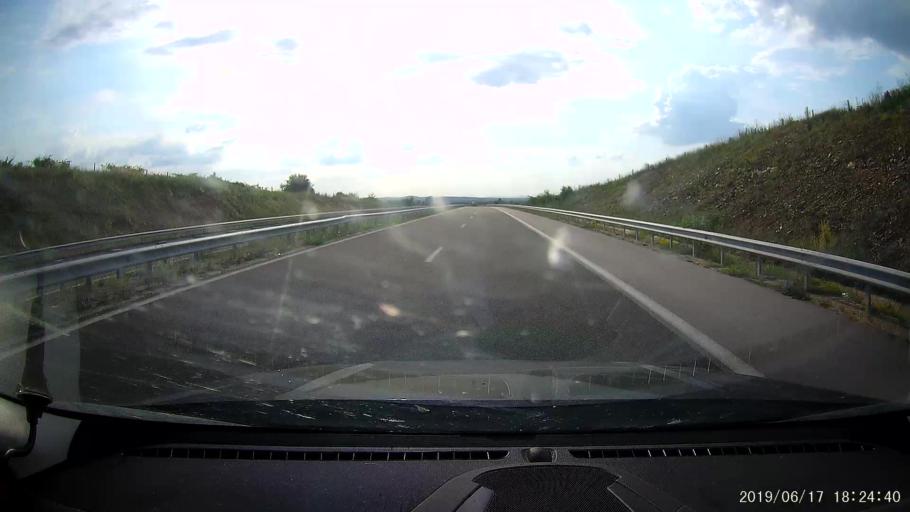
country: BG
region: Khaskovo
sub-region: Obshtina Dimitrovgrad
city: Dimitrovgrad
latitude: 41.9867
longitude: 25.6847
